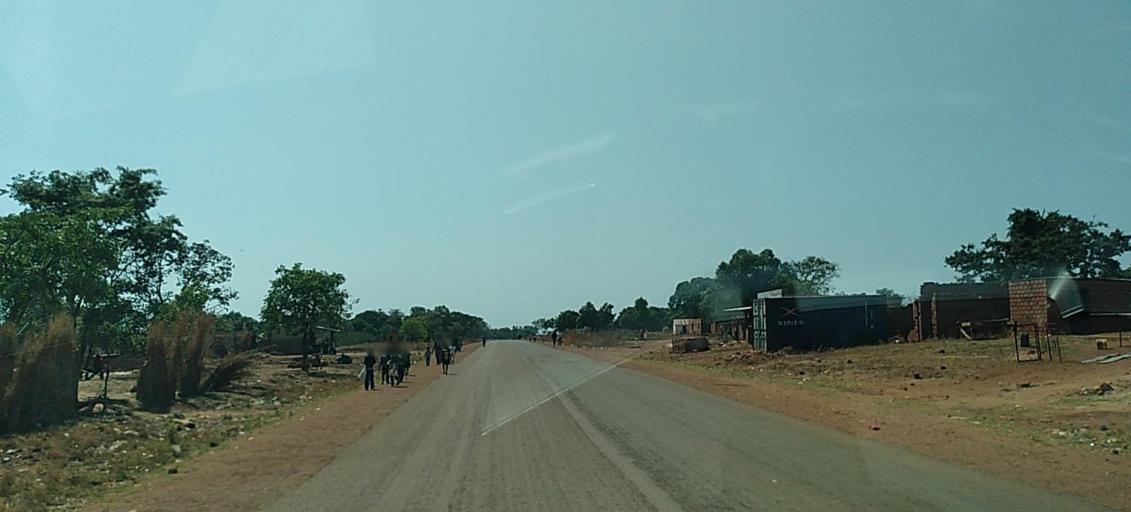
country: ZM
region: North-Western
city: Solwezi
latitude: -12.1107
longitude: 25.5011
